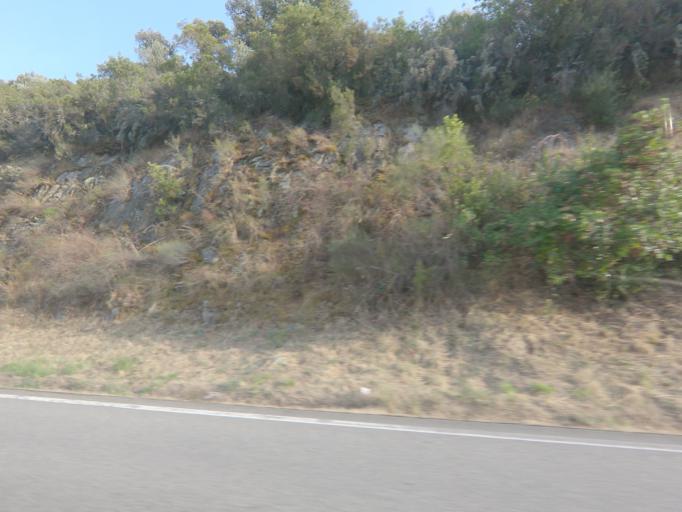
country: PT
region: Viseu
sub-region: Armamar
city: Armamar
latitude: 41.1609
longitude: -7.6535
